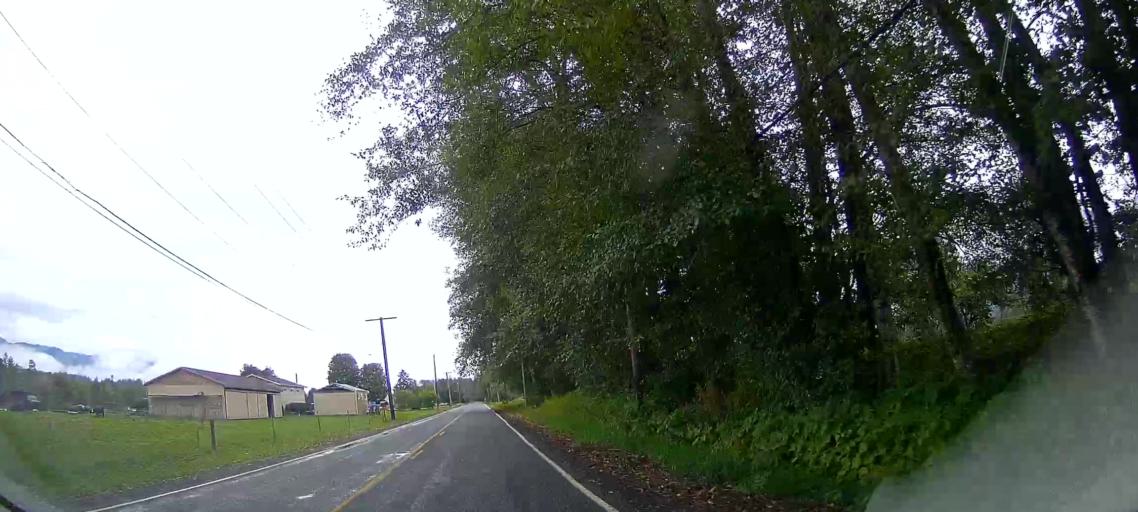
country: US
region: Washington
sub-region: Skagit County
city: Sedro-Woolley
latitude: 48.5271
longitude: -122.0377
